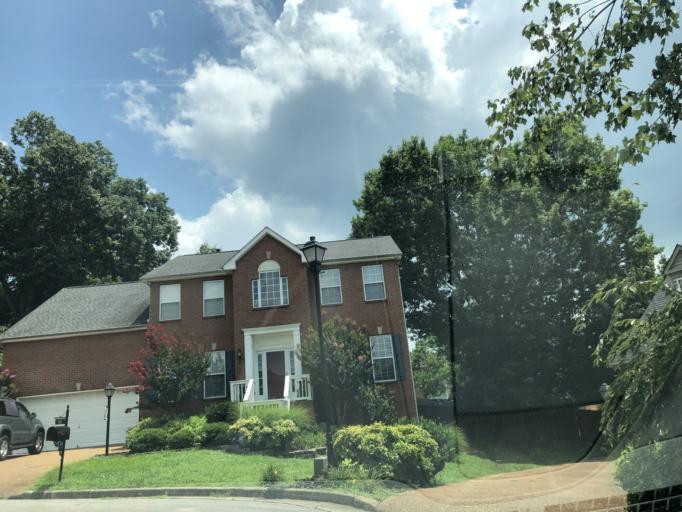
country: US
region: Tennessee
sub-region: Williamson County
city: Brentwood Estates
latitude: 36.0148
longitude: -86.7146
